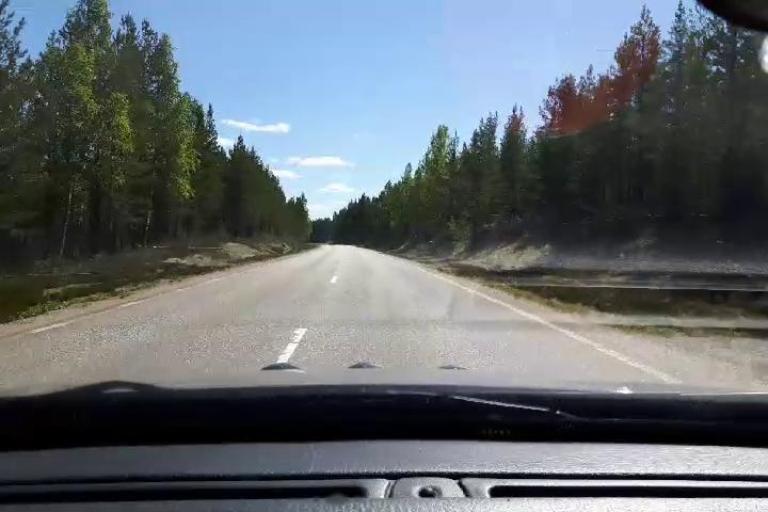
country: SE
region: Vaesternorrland
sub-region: Ange Kommun
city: Ange
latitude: 62.0701
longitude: 15.1039
